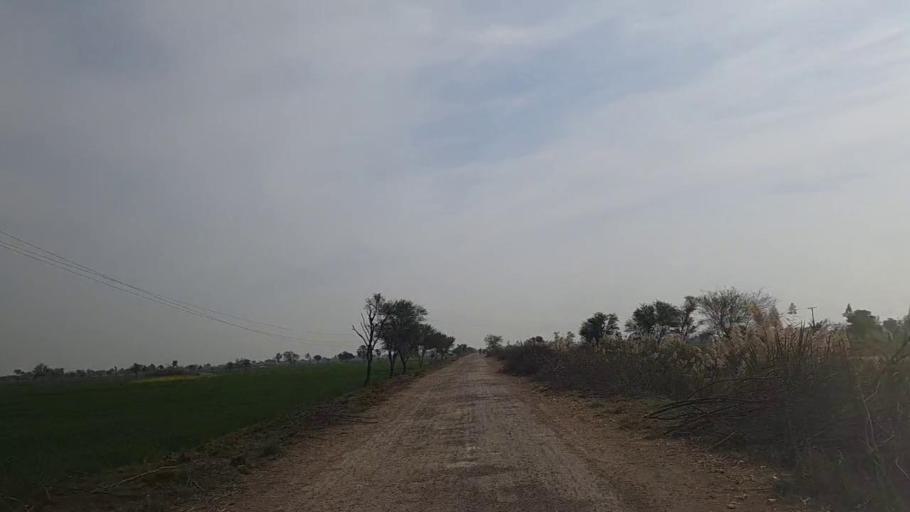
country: PK
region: Sindh
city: Daur
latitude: 26.4489
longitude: 68.4160
